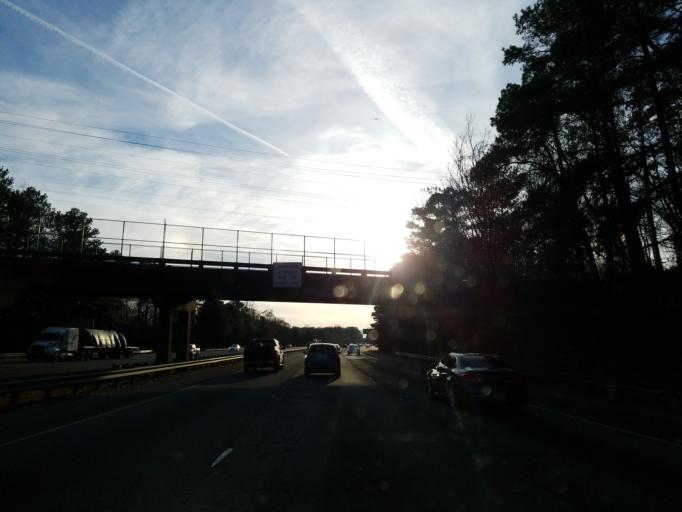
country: US
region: Georgia
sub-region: Douglas County
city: Douglasville
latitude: 33.7373
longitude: -84.7296
